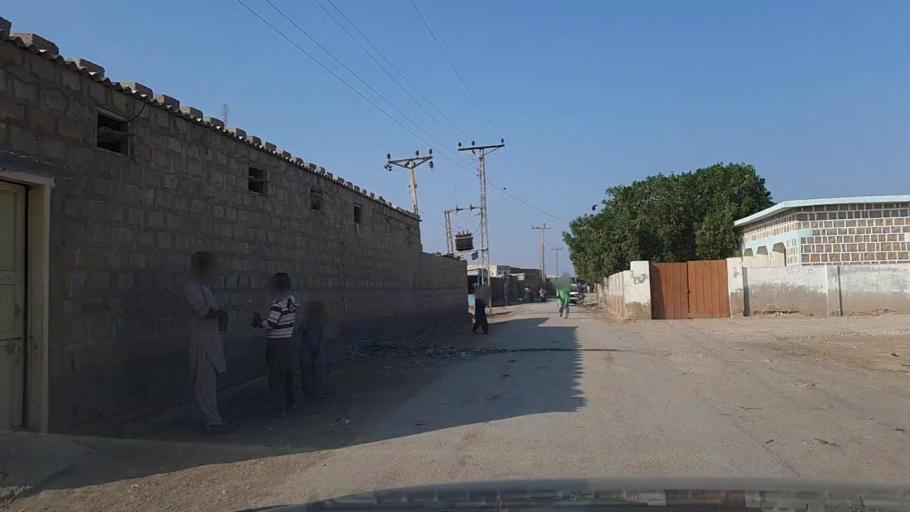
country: PK
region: Sindh
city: Keti Bandar
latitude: 24.1424
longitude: 67.4510
